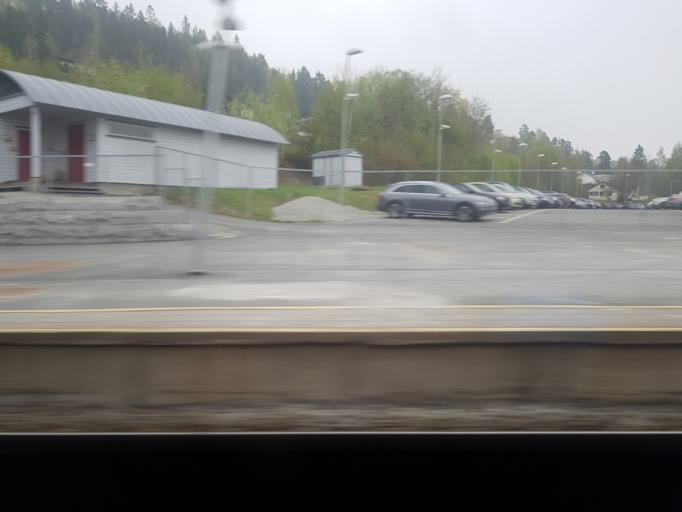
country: NO
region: Buskerud
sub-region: Lier
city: Lierbyen
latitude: 59.7639
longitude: 10.2852
